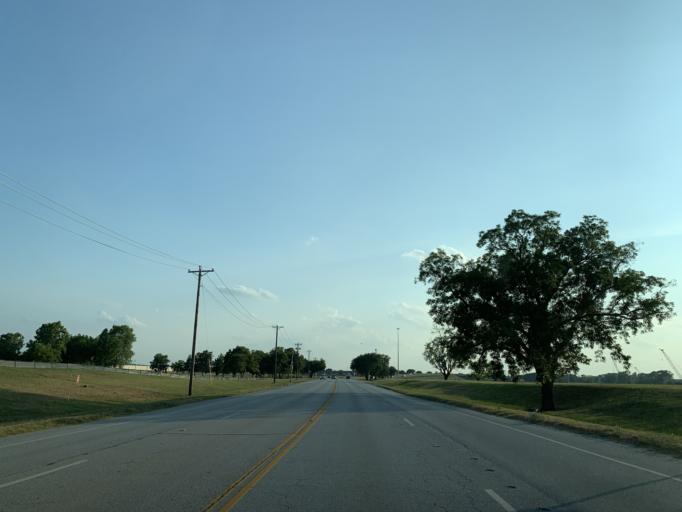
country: US
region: Texas
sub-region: Tarrant County
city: Richland Hills
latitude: 32.8010
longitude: -97.2056
